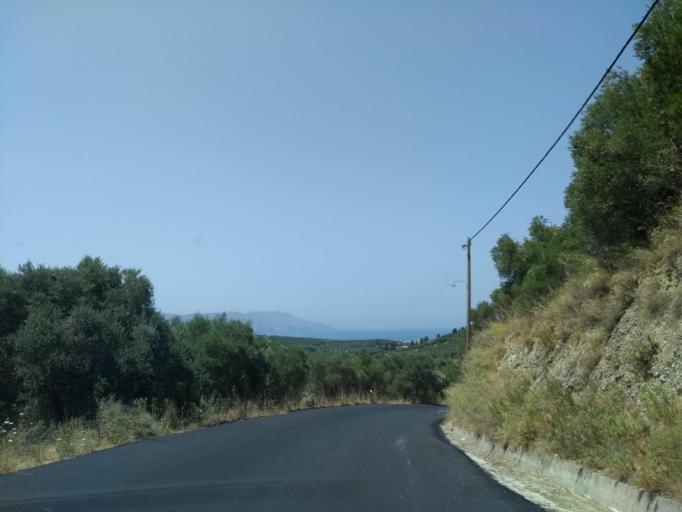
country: GR
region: Crete
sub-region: Nomos Chanias
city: Georgioupolis
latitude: 35.3248
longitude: 24.2999
